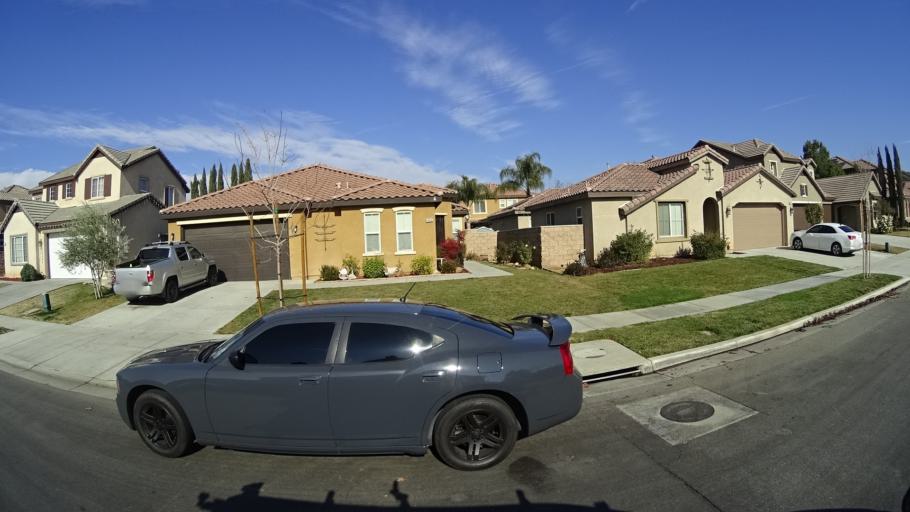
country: US
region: California
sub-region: Kern County
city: Oildale
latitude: 35.4055
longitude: -118.8943
